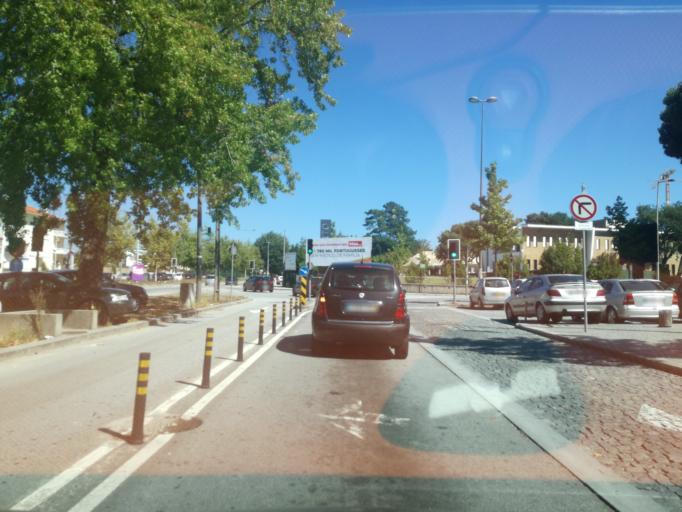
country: PT
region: Porto
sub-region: Matosinhos
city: Sao Mamede de Infesta
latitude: 41.1822
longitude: -8.5978
